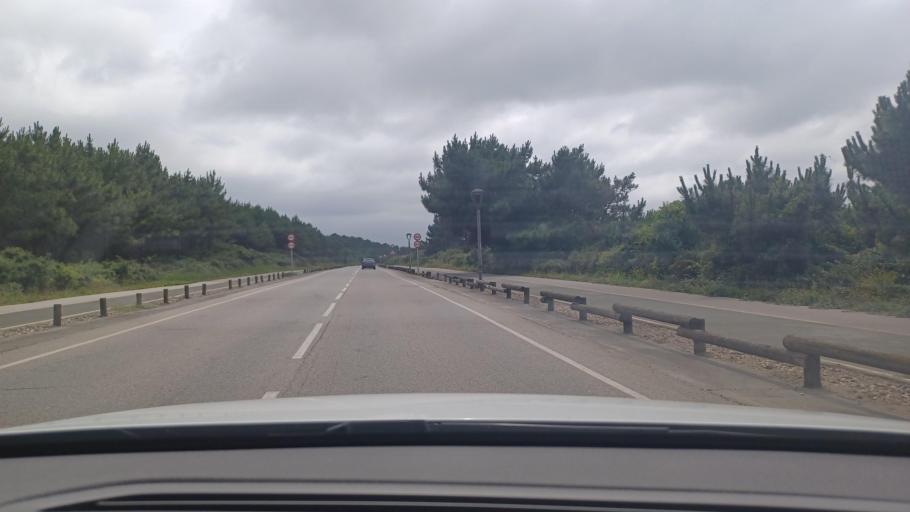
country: ES
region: Asturias
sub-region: Province of Asturias
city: Aviles
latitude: 43.5827
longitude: -5.9439
